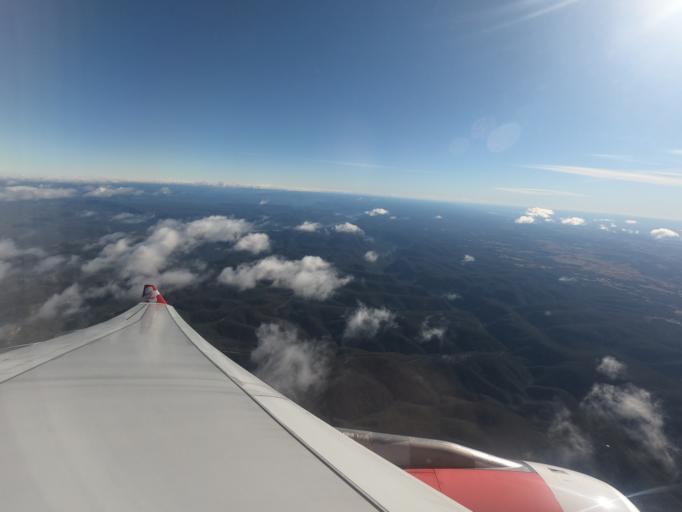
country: AU
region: New South Wales
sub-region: Wollondilly
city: Buxton
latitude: -34.2700
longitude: 150.4443
